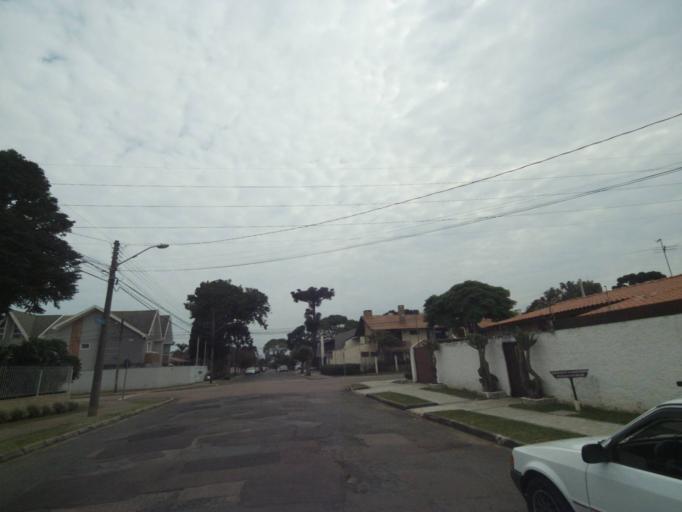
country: BR
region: Parana
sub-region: Curitiba
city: Curitiba
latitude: -25.4647
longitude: -49.3059
